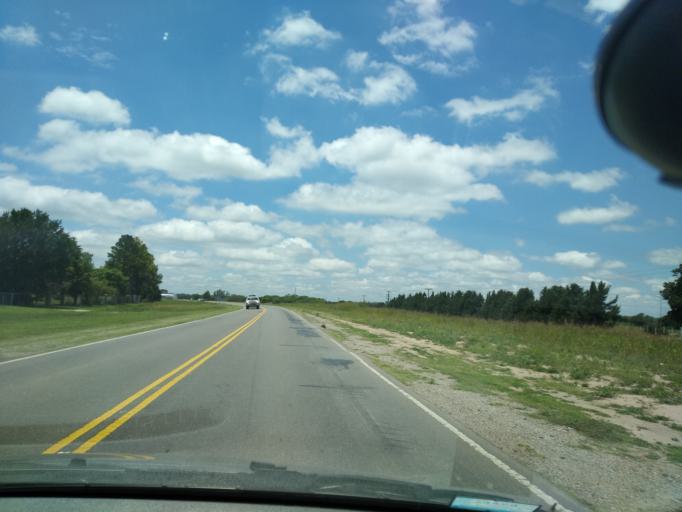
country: AR
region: Cordoba
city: Alta Gracia
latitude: -31.6580
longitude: -64.3595
